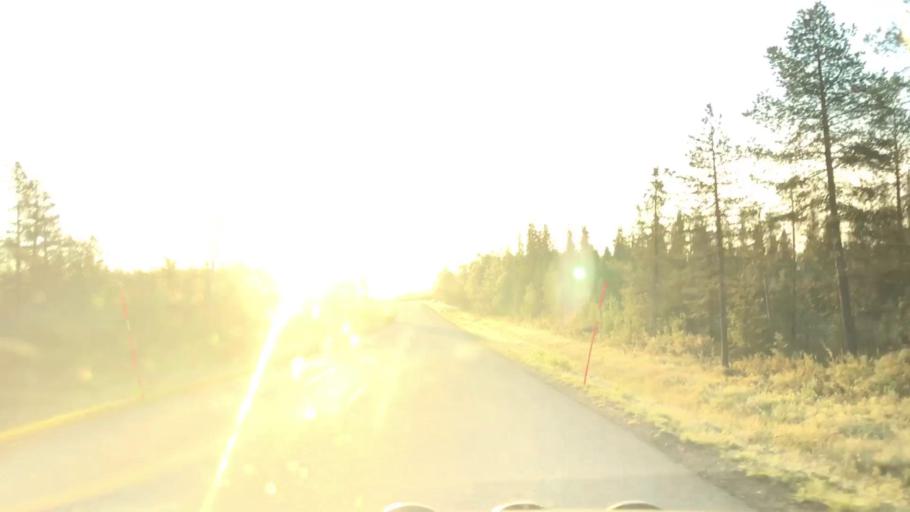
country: SE
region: Norrbotten
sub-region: Gallivare Kommun
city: Malmberget
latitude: 67.6507
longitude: 21.0274
